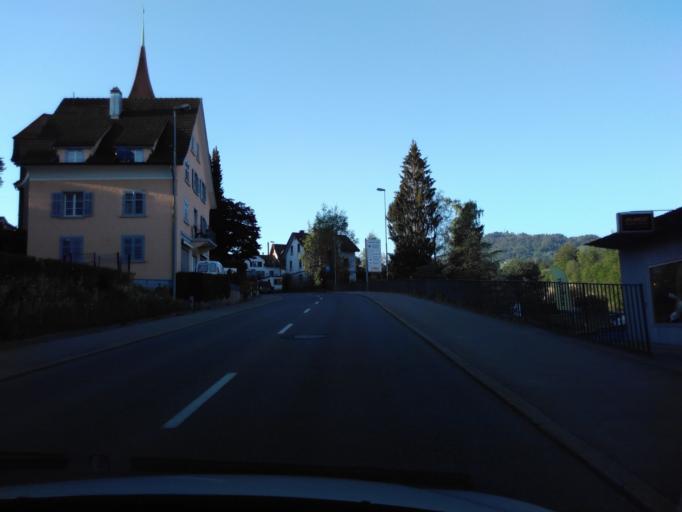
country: CH
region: Zurich
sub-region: Bezirk Hinwil
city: Tann / Tann (Dorfkern)
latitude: 47.2627
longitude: 8.8516
